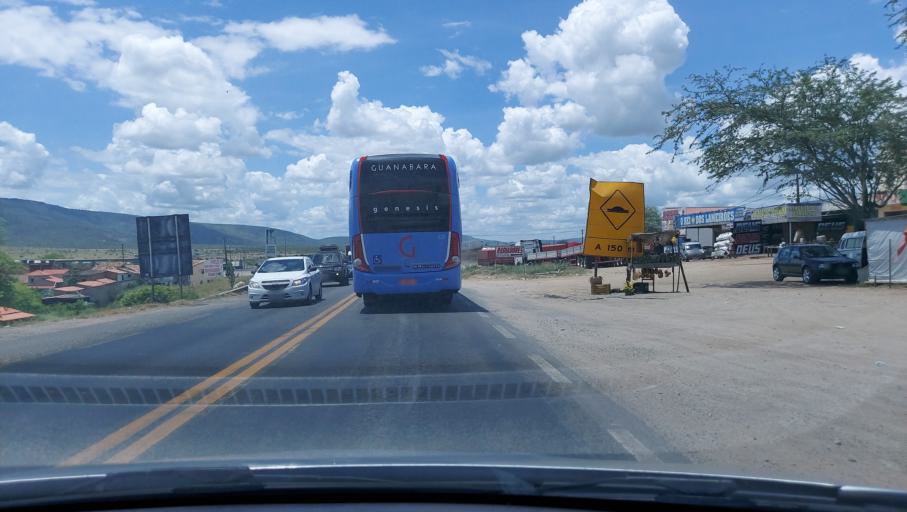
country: BR
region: Bahia
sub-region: Castro Alves
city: Castro Alves
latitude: -12.5820
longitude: -39.5194
